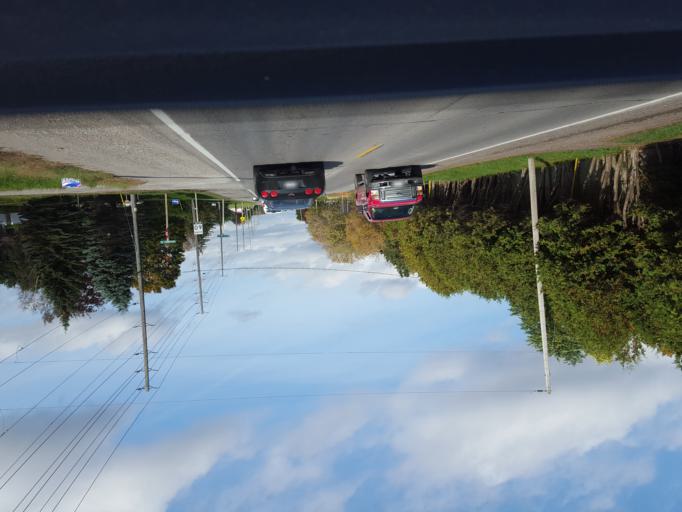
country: CA
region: Ontario
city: Oshawa
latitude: 43.9632
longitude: -78.7477
